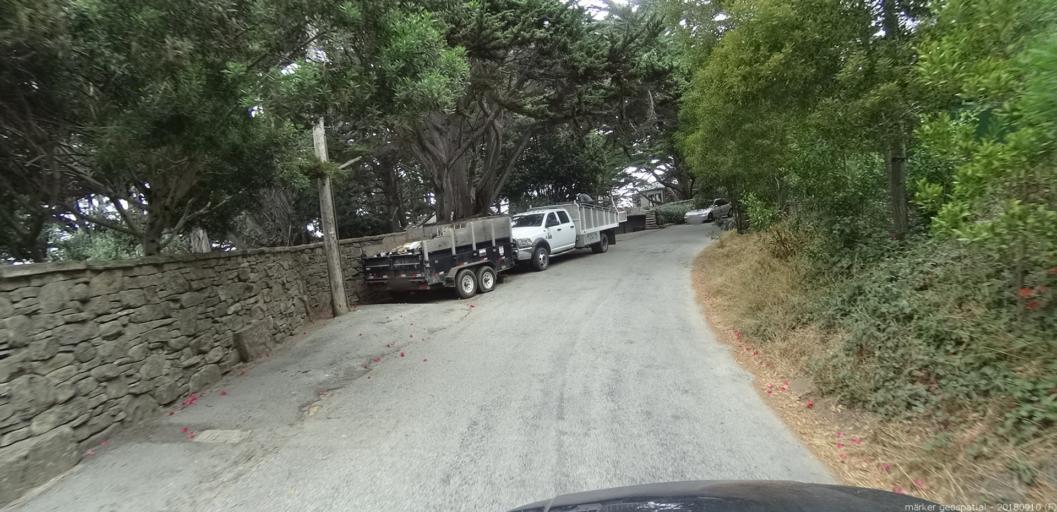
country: US
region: California
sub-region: Monterey County
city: Carmel-by-the-Sea
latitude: 36.4953
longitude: -121.9388
